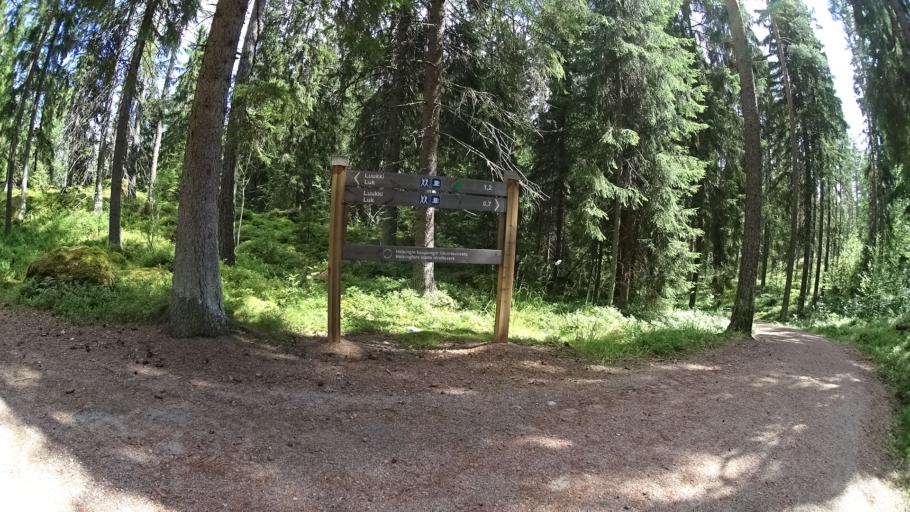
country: FI
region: Uusimaa
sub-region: Helsinki
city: Kauniainen
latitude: 60.3175
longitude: 24.6817
